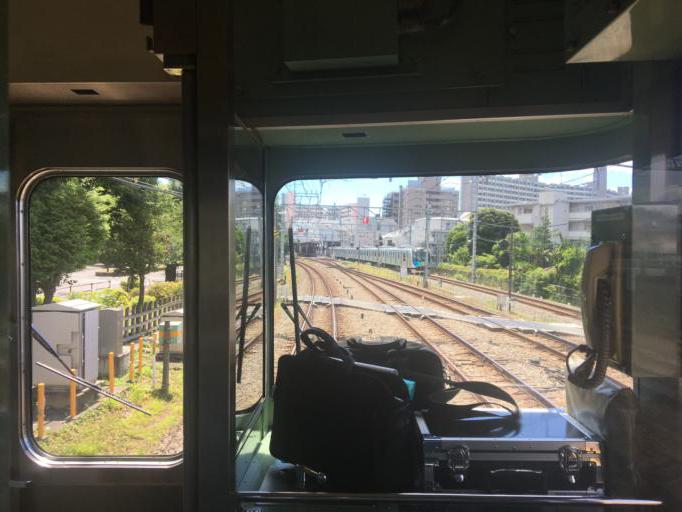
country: JP
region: Tokyo
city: Higashimurayama-shi
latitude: 35.7385
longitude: 139.4856
